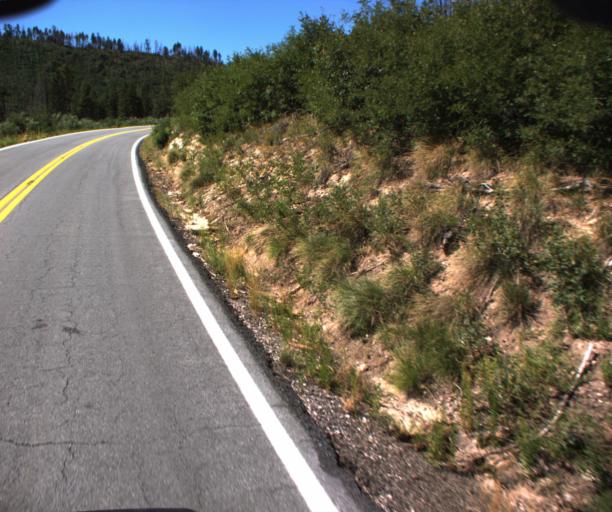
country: US
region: Arizona
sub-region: Apache County
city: Eagar
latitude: 33.8201
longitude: -109.1551
